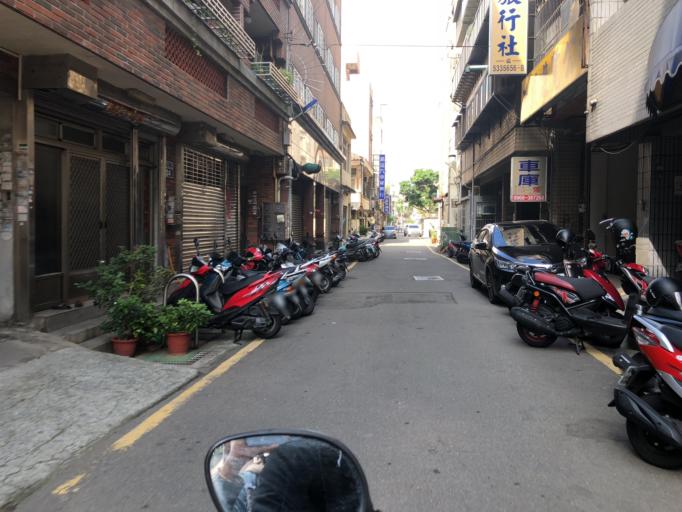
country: TW
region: Taiwan
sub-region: Hsinchu
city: Hsinchu
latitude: 24.8083
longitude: 120.9801
